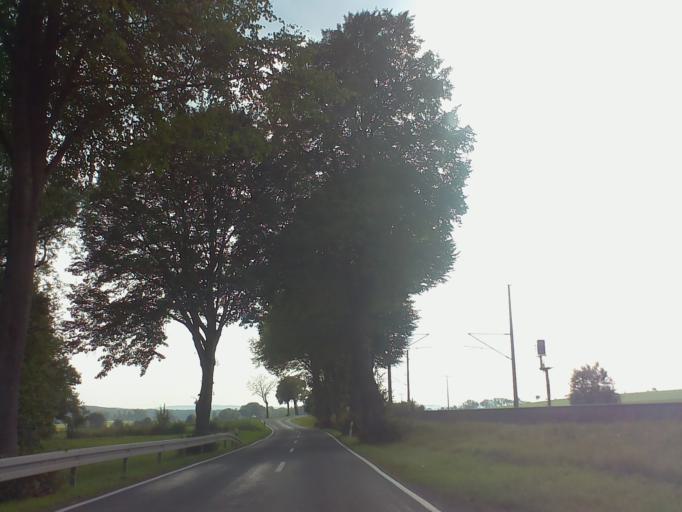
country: DE
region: Thuringia
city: Gerstungen
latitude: 50.9900
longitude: 10.0963
